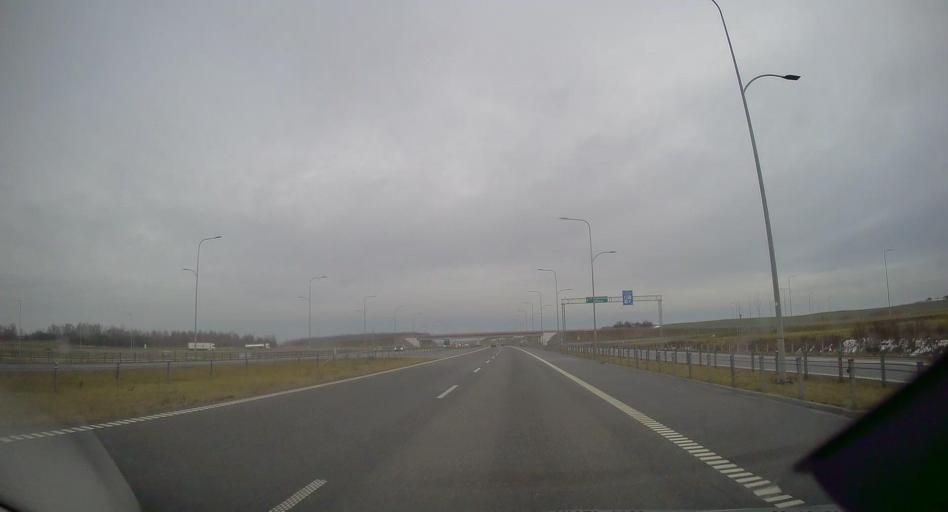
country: PL
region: Silesian Voivodeship
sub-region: Powiat czestochowski
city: Mykanow
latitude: 50.8770
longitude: 19.1450
